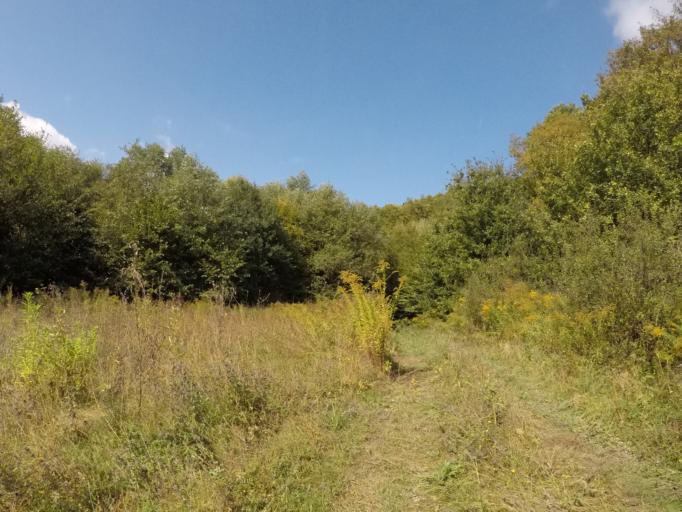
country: SK
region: Presovsky
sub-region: Okres Presov
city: Presov
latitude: 48.9339
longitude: 21.1620
